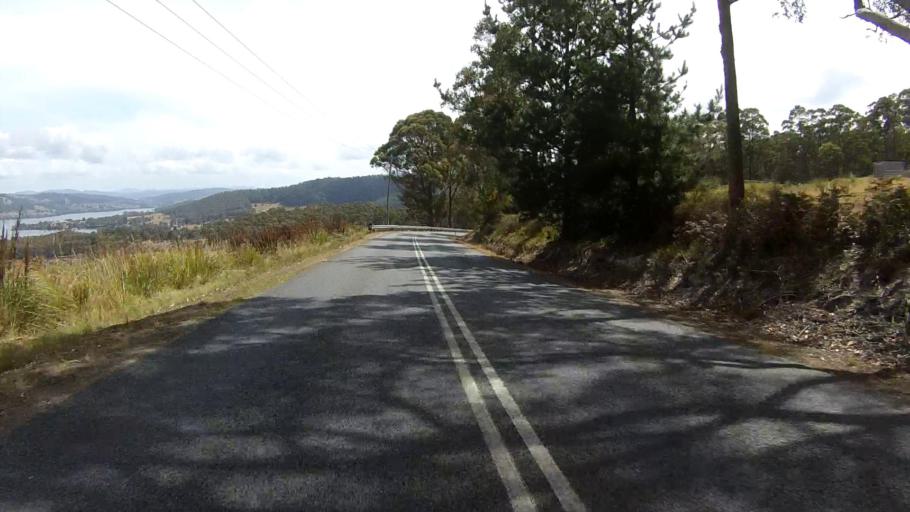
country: AU
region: Tasmania
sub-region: Huon Valley
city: Cygnet
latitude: -43.2259
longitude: 147.1278
